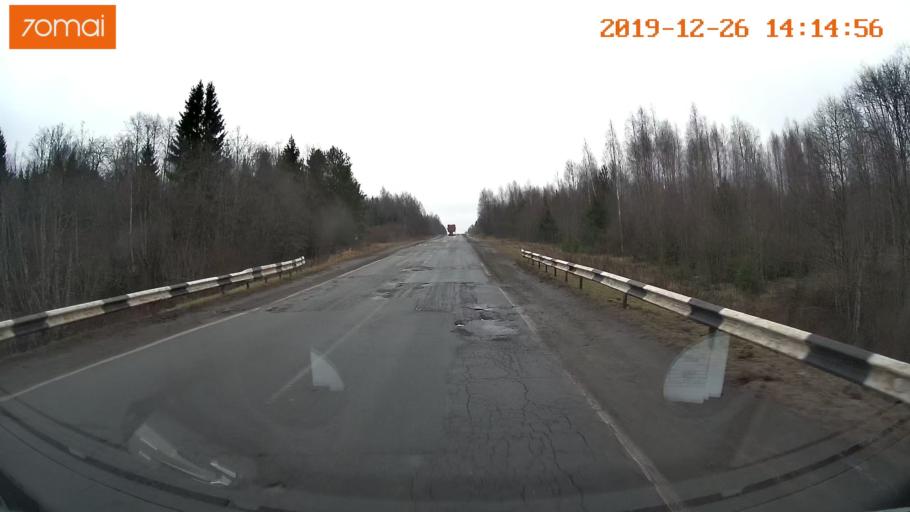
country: RU
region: Jaroslavl
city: Poshekhon'ye
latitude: 58.5148
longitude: 39.0369
